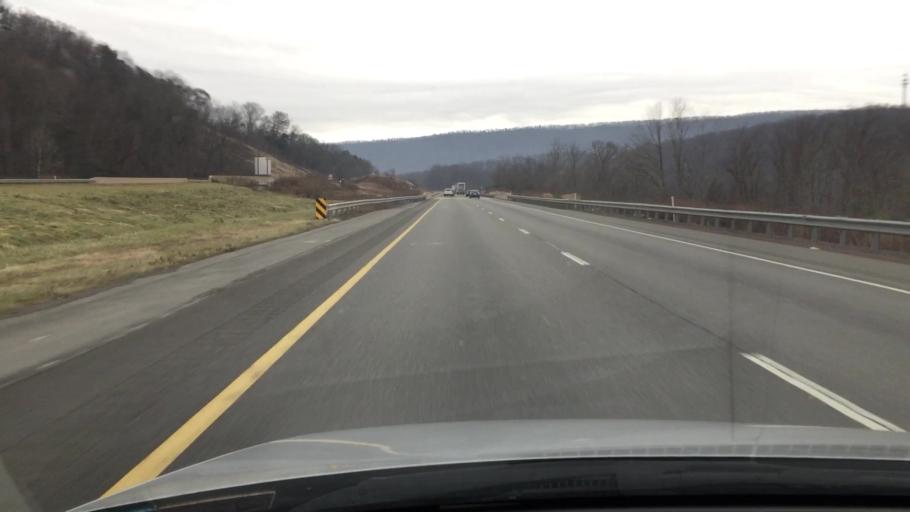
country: US
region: Pennsylvania
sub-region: Columbia County
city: Mifflinville
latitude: 41.0157
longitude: -76.3044
